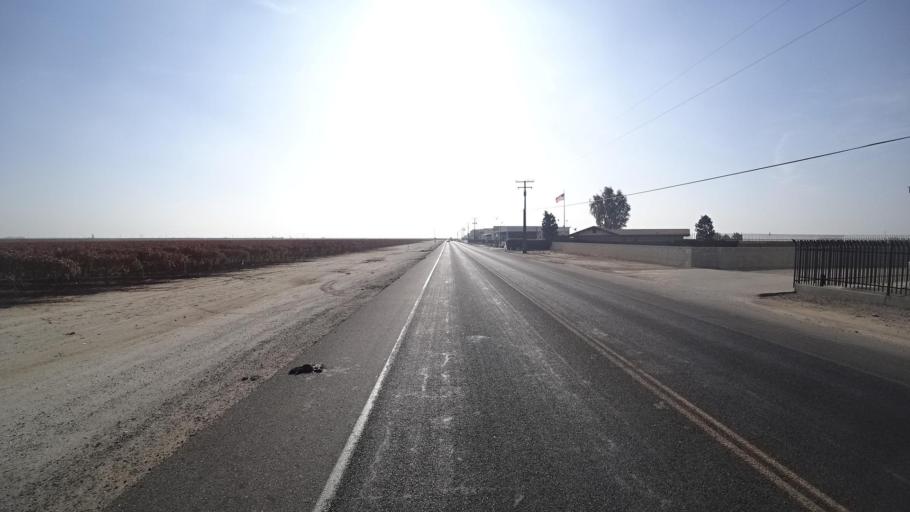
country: US
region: California
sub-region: Tulare County
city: Richgrove
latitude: 35.7448
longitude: -119.1427
